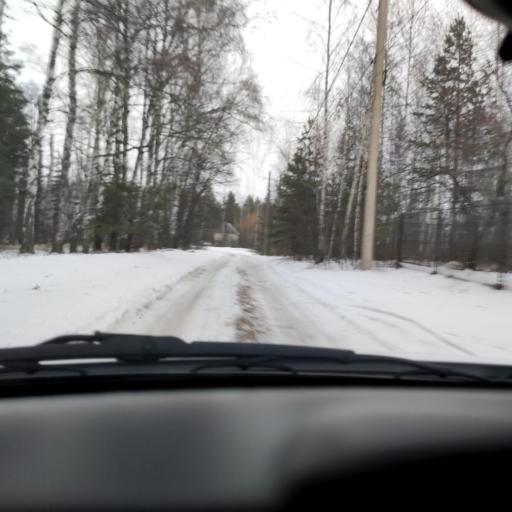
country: RU
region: Voronezj
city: Ramon'
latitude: 51.8808
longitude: 39.2659
